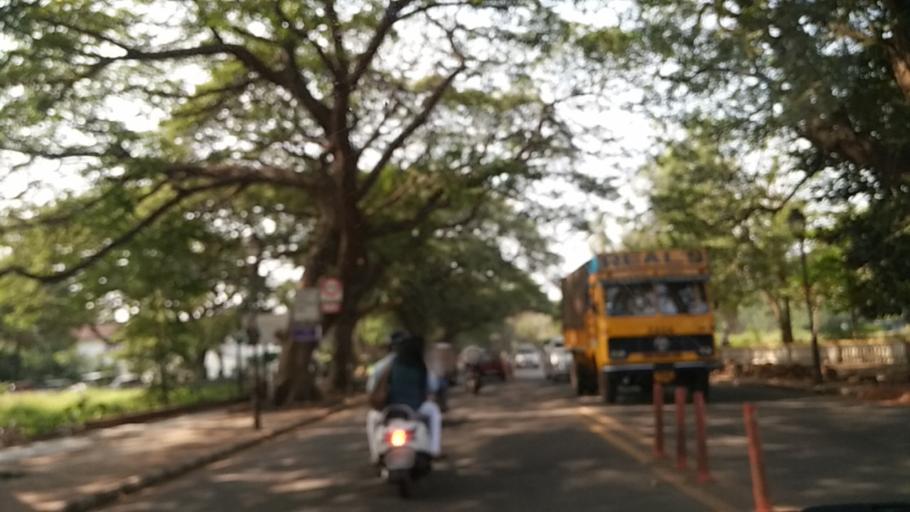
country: IN
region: Goa
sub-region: North Goa
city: Panaji
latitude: 15.4899
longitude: 73.8150
